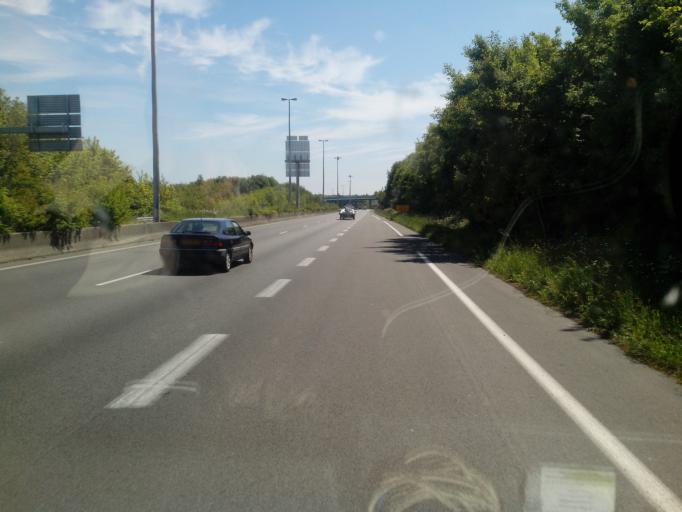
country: FR
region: Nord-Pas-de-Calais
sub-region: Departement du Pas-de-Calais
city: Saint-Martin-Boulogne
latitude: 50.7445
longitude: 1.6280
